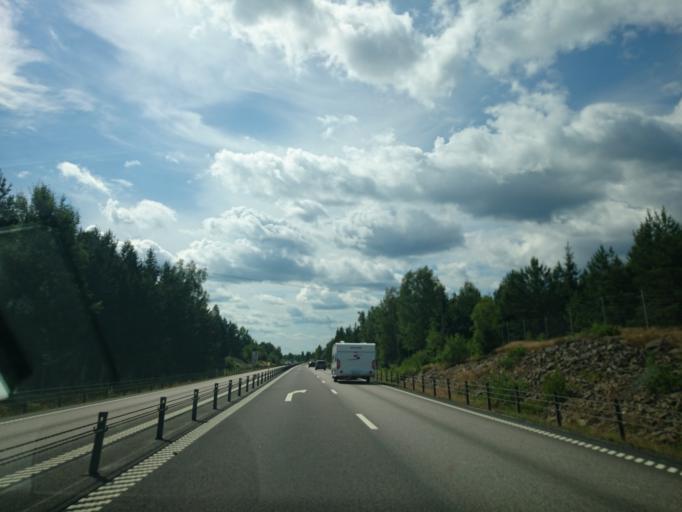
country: SE
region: Kalmar
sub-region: Oskarshamns Kommun
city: Oskarshamn
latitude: 57.2240
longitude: 16.4368
